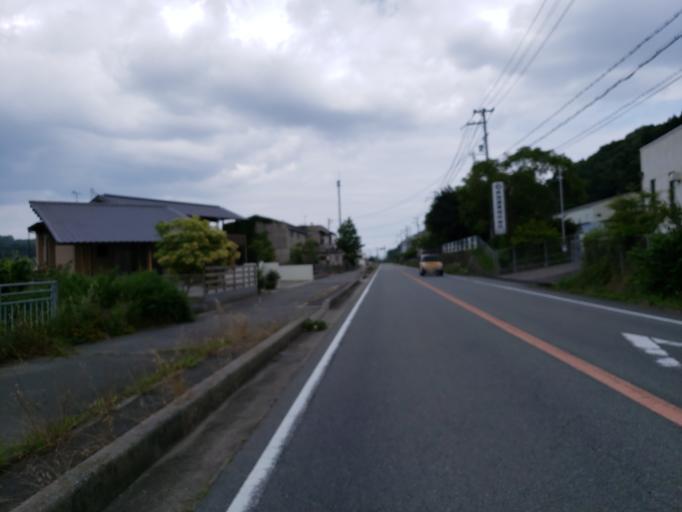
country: JP
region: Hyogo
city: Aioi
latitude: 34.7818
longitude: 134.5373
